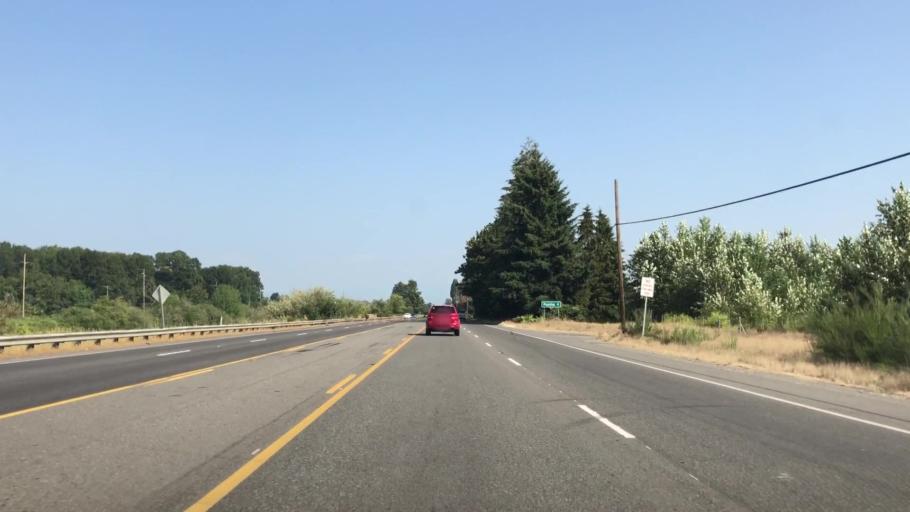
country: US
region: Washington
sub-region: Pierce County
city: Fife
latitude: 47.2326
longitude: -122.3845
